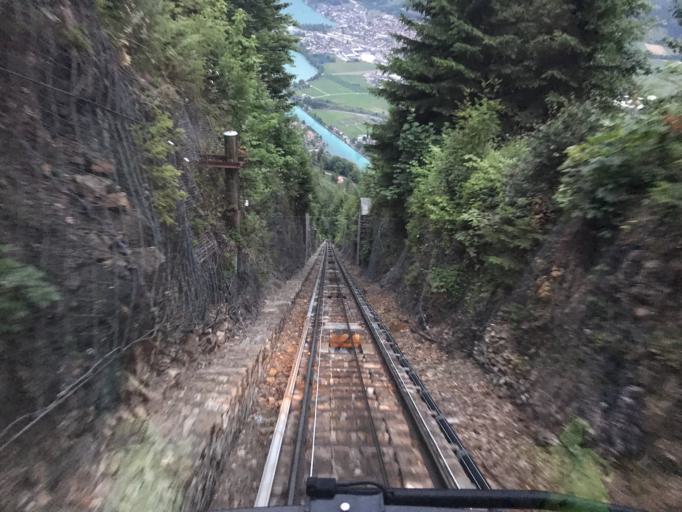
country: CH
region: Bern
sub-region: Interlaken-Oberhasli District
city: Unterseen
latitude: 46.6981
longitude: 7.8557
